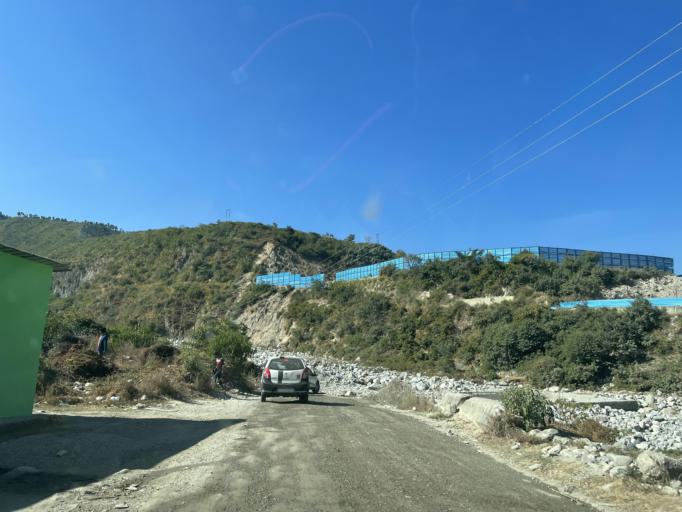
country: IN
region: Uttarakhand
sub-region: Almora
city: Ranikhet
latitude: 29.5501
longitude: 79.4025
